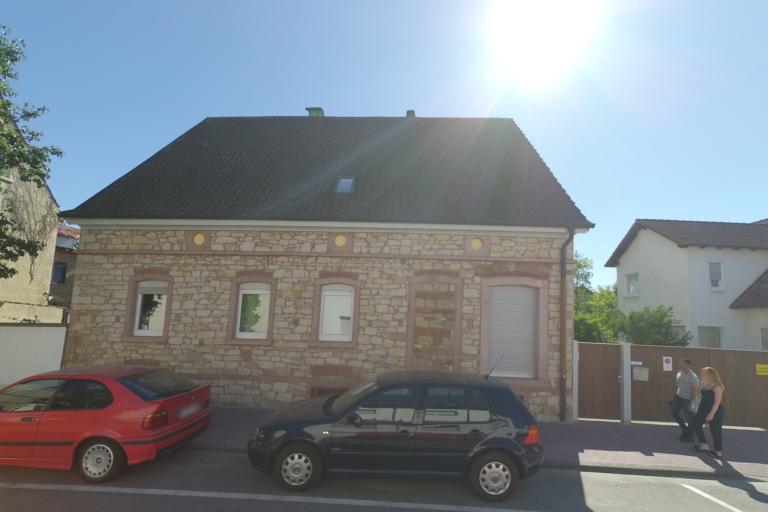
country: DE
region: Hesse
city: Viernheim
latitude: 49.5407
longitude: 8.5785
